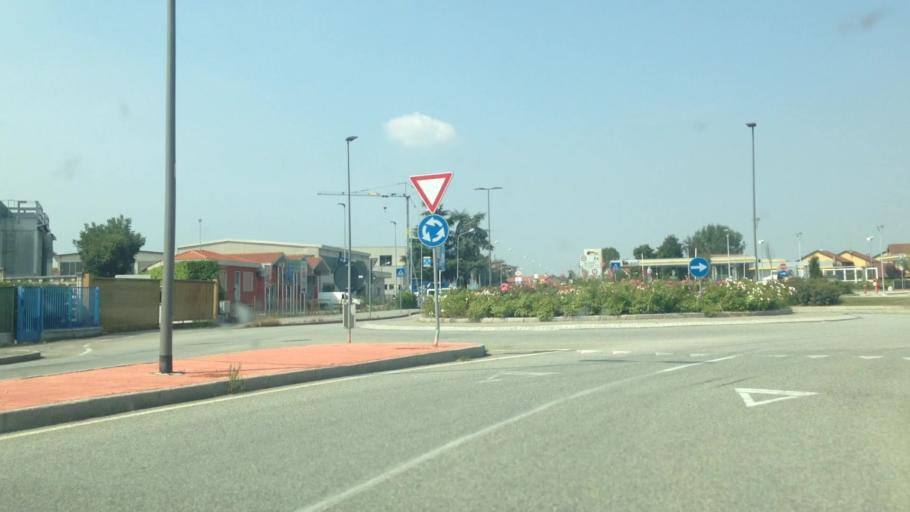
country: IT
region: Piedmont
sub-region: Provincia di Alessandria
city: Casale Monferrato
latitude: 45.1286
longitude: 8.4771
